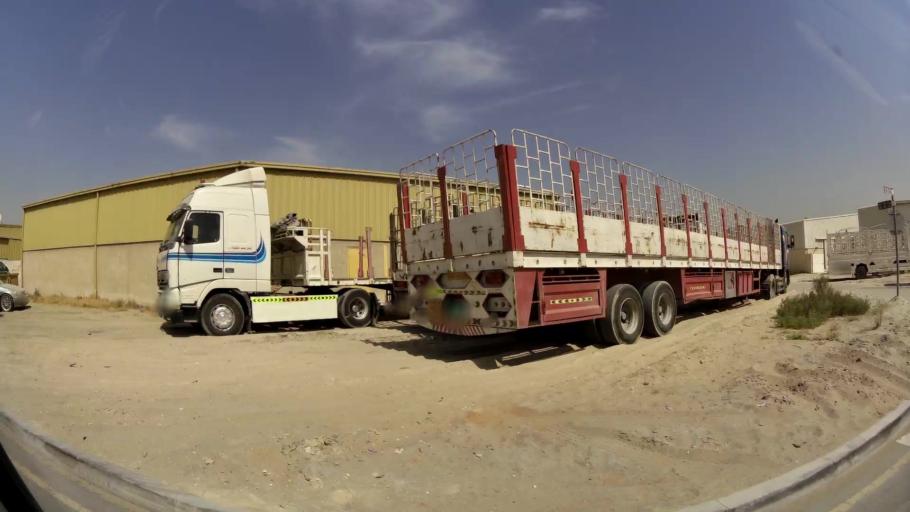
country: AE
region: Ash Shariqah
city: Sharjah
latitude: 25.2772
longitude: 55.3911
